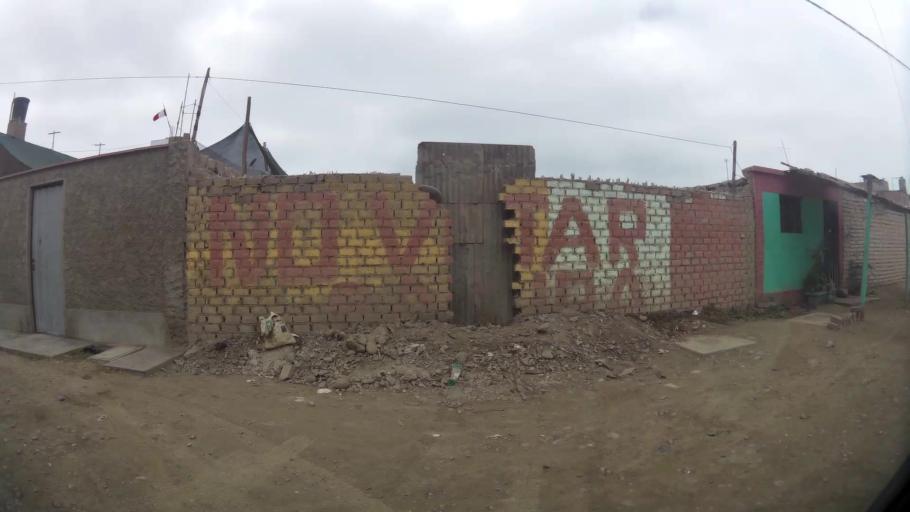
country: PE
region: Lima
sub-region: Provincia de Huaral
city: Huaral
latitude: -11.4943
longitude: -77.2024
